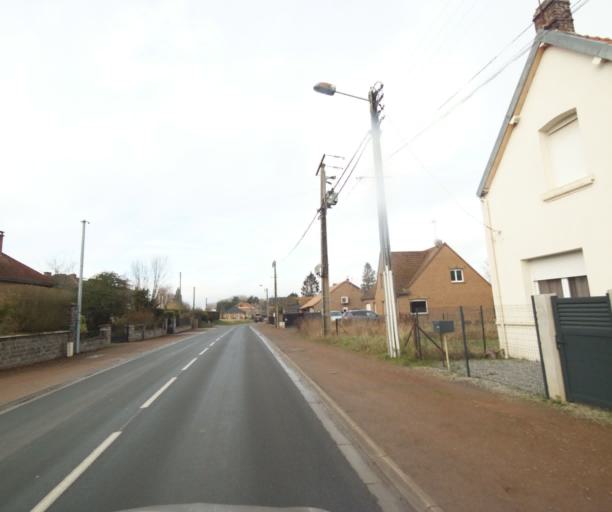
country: FR
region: Nord-Pas-de-Calais
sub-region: Departement du Nord
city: Saulzoir
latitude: 50.2668
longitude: 3.4704
